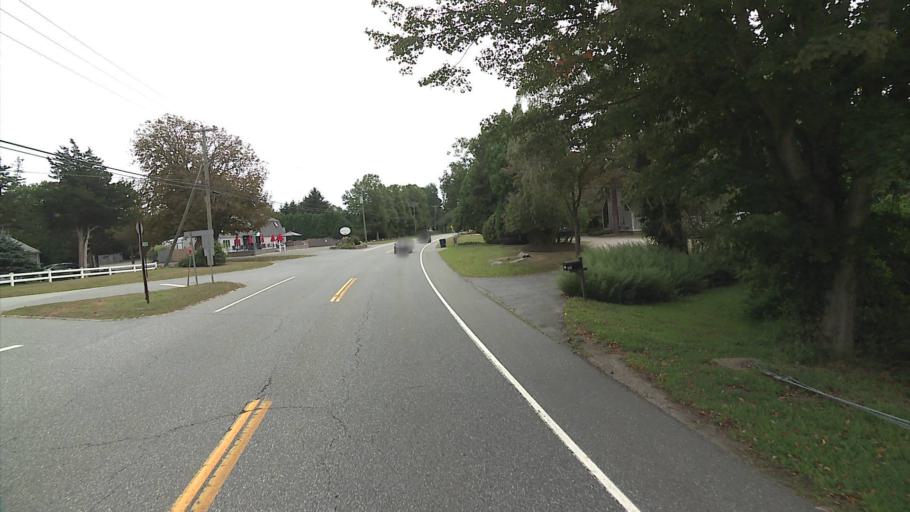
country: US
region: Connecticut
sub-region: Middlesex County
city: Old Saybrook Center
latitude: 41.2952
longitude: -72.3159
